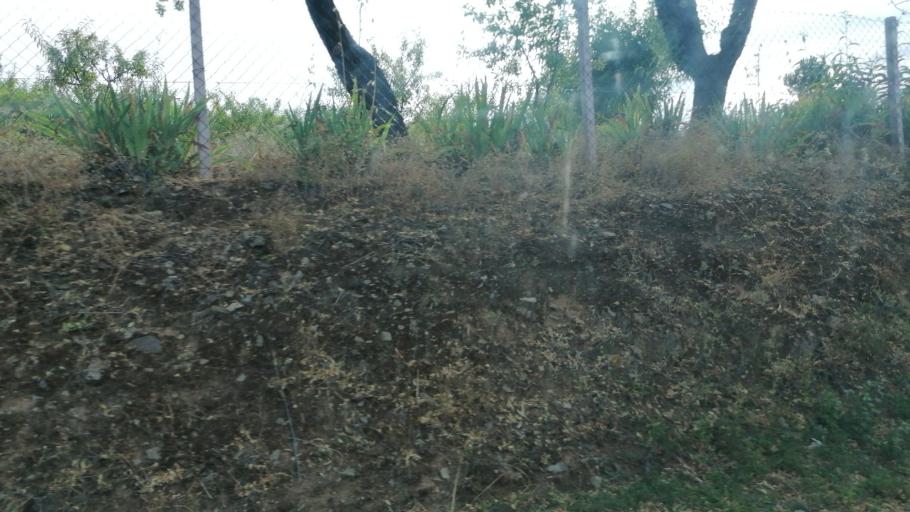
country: PT
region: Viseu
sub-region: Sao Joao da Pesqueira
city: Sao Joao da Pesqueira
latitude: 41.1409
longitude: -7.3968
